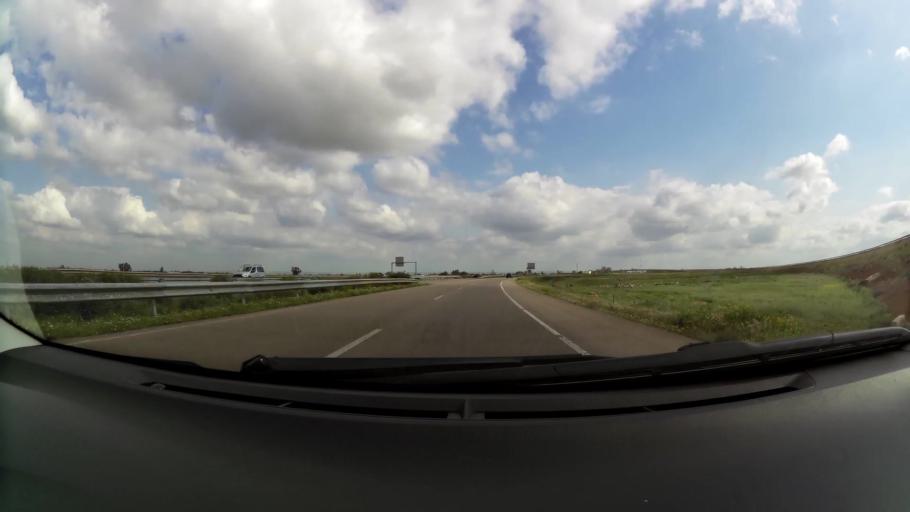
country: MA
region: Chaouia-Ouardigha
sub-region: Settat Province
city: Berrechid
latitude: 33.2882
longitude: -7.5478
